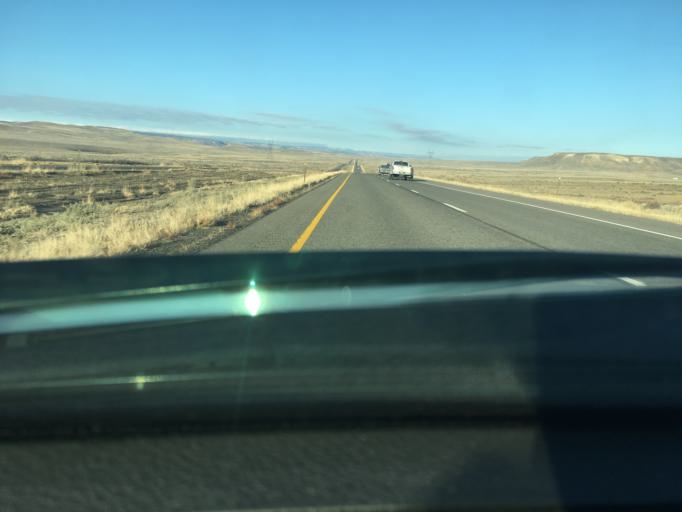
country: US
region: Colorado
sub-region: Delta County
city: Delta
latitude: 38.7575
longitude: -108.1823
